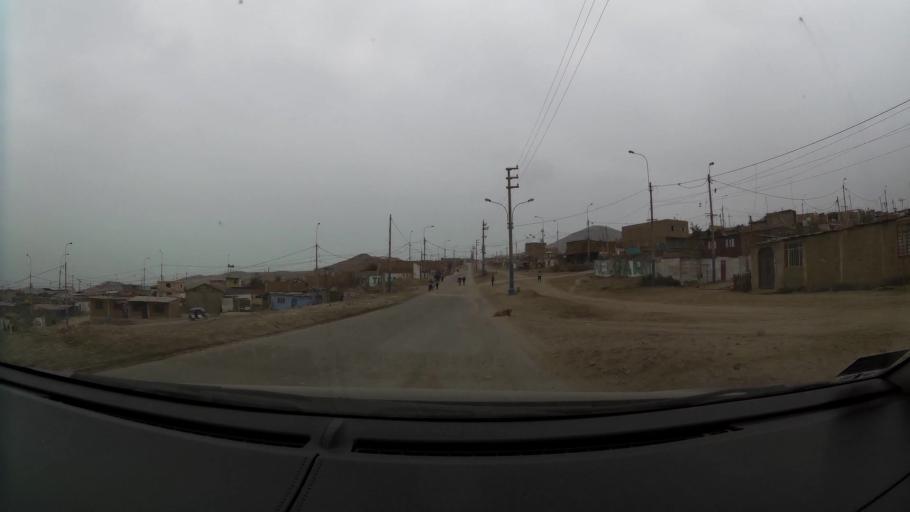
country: PE
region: Lima
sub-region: Lima
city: Santa Rosa
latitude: -11.8366
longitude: -77.1626
